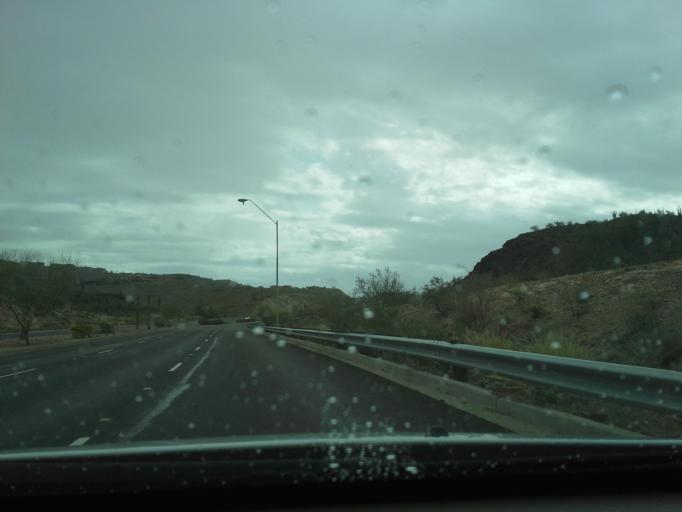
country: US
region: Arizona
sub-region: Maricopa County
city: Fountain Hills
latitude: 33.5787
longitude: -111.7711
